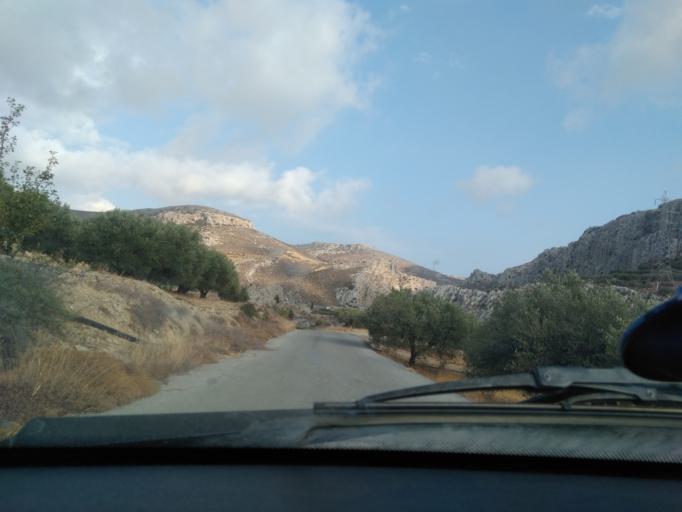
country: GR
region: Crete
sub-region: Nomos Lasithiou
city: Makry-Gialos
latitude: 35.0465
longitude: 26.0527
